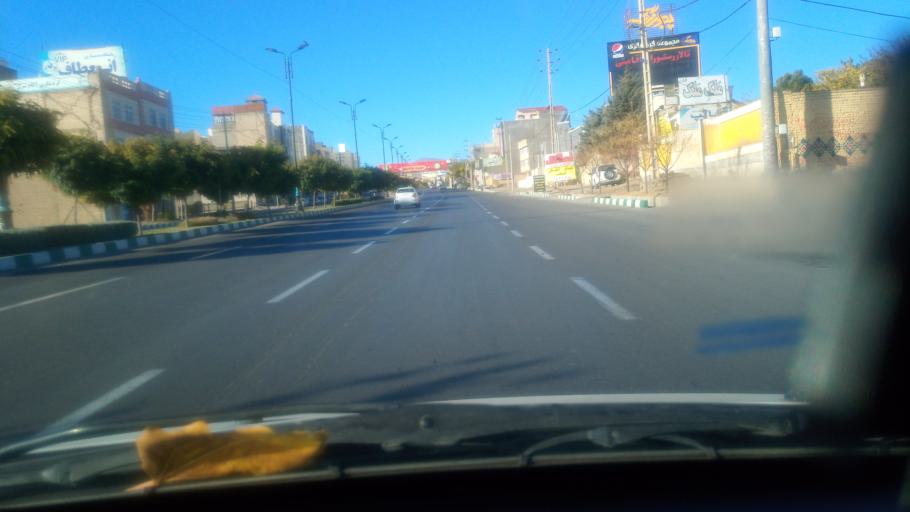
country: IR
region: Razavi Khorasan
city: Torqabeh
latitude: 36.3157
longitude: 59.3802
